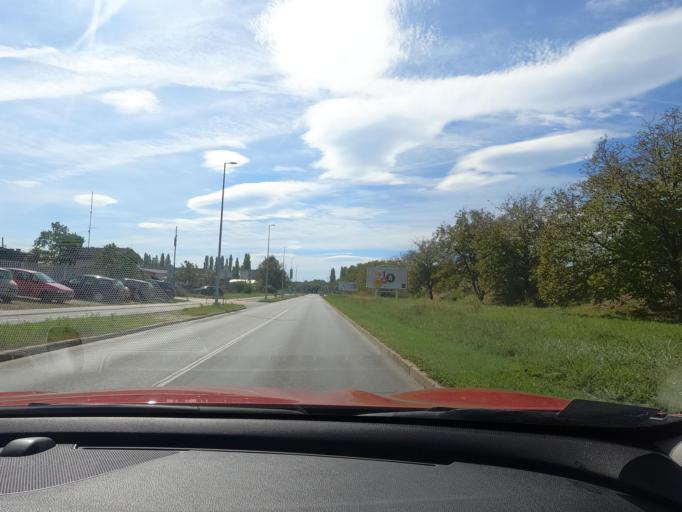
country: HR
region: Sisacko-Moslavacka
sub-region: Grad Sisak
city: Sisak
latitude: 45.4849
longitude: 16.3797
